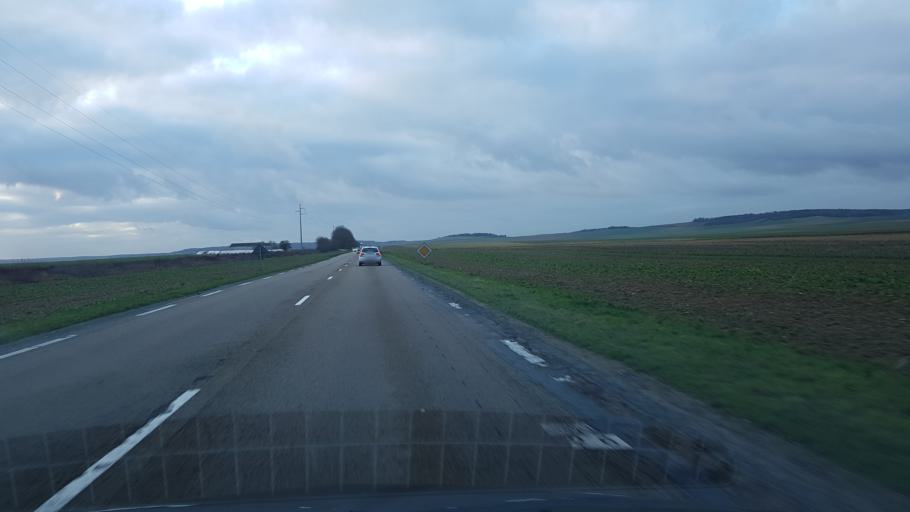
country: FR
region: Champagne-Ardenne
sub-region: Departement de la Marne
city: Sezanne
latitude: 48.7228
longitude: 3.7977
